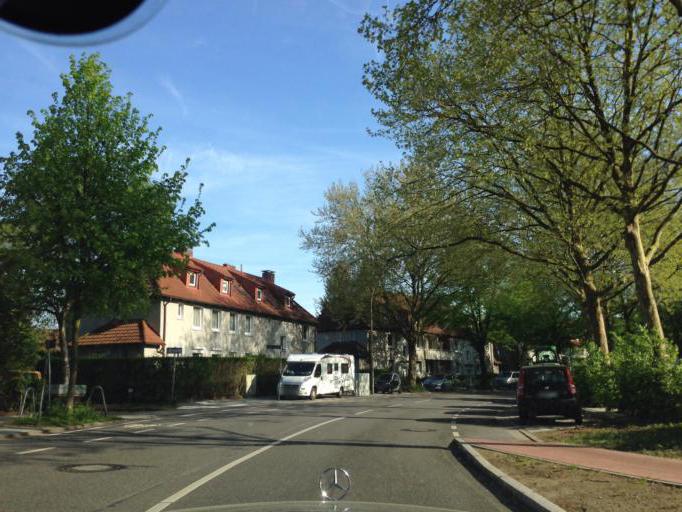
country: DE
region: Hamburg
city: Marienthal
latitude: 53.5887
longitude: 10.0786
